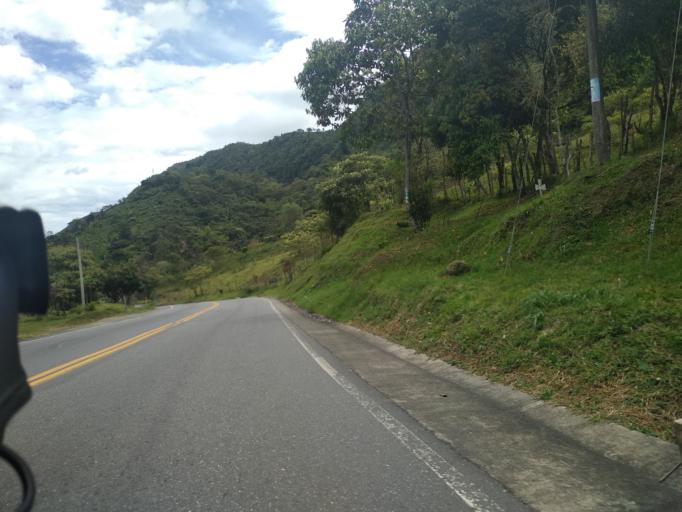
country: CO
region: Cauca
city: Rosas
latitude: 2.2626
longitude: -76.7437
